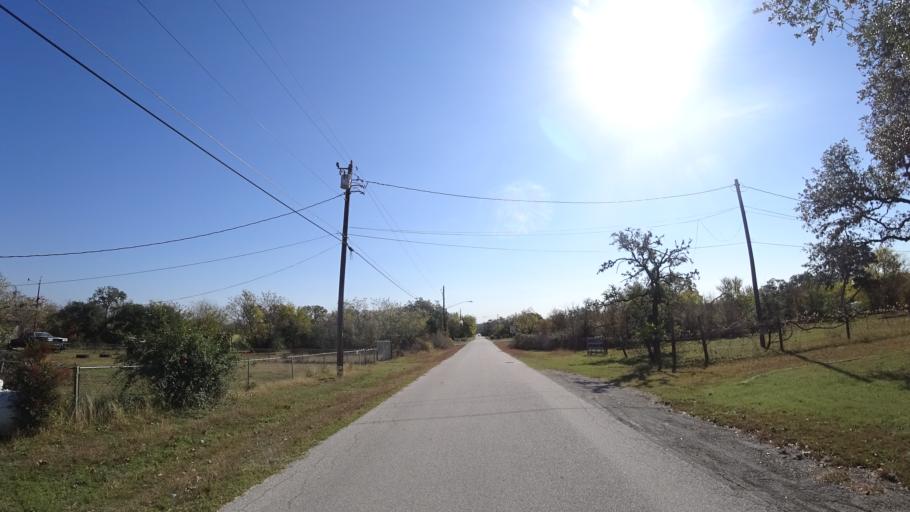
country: US
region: Texas
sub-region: Travis County
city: Barton Creek
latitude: 30.2304
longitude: -97.8589
